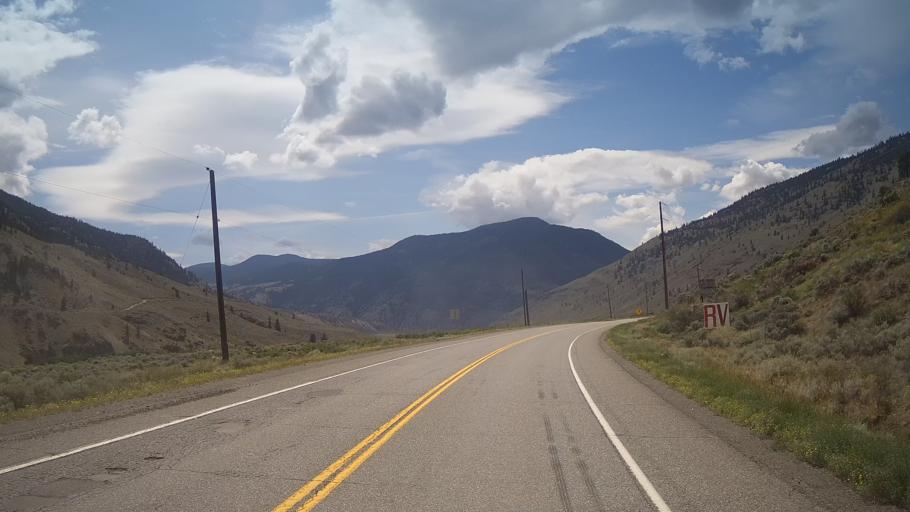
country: CA
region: British Columbia
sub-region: Thompson-Nicola Regional District
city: Ashcroft
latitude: 50.4603
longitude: -121.3022
